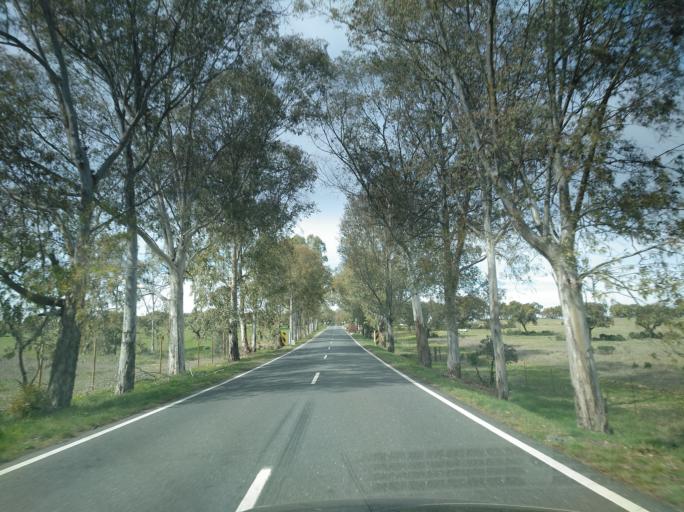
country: PT
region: Beja
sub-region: Mertola
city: Mertola
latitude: 37.7304
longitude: -7.7677
